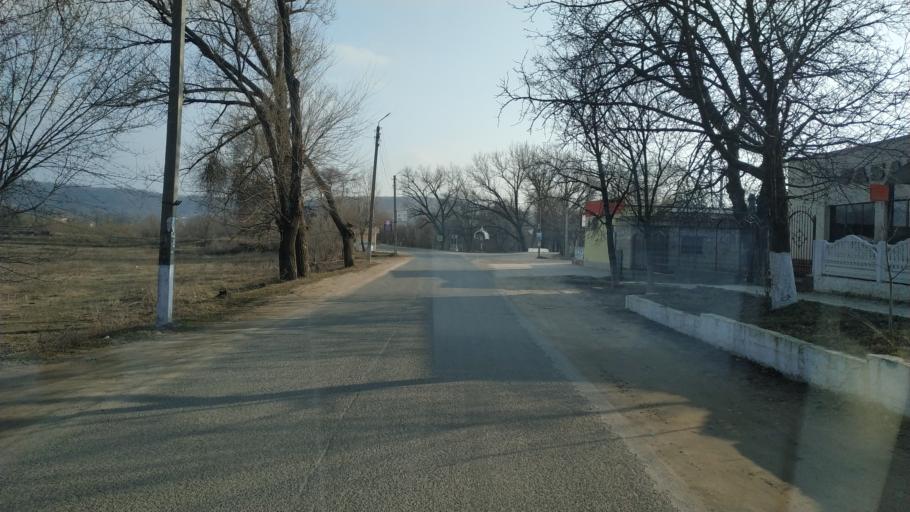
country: MD
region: Hincesti
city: Dancu
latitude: 46.7661
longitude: 28.3459
